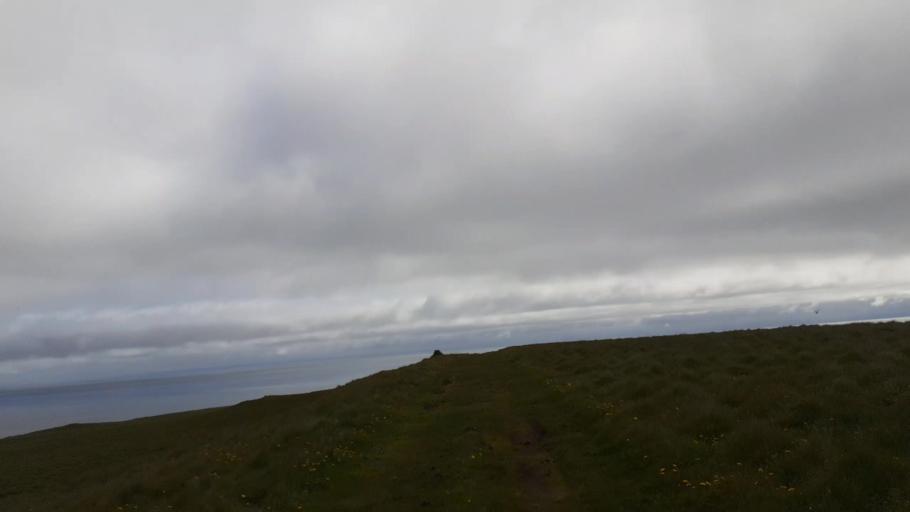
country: IS
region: Northeast
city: Dalvik
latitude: 66.5408
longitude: -17.9843
